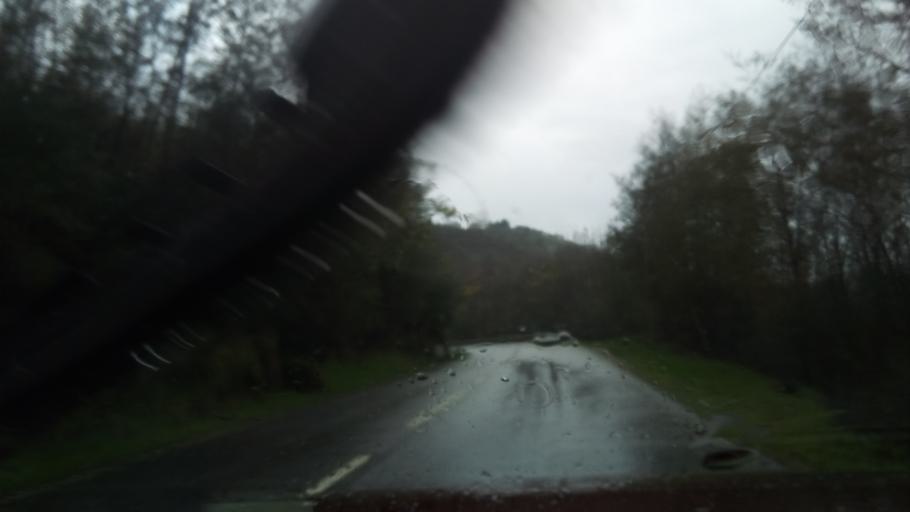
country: PT
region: Guarda
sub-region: Fornos de Algodres
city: Fornos de Algodres
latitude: 40.6171
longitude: -7.5004
